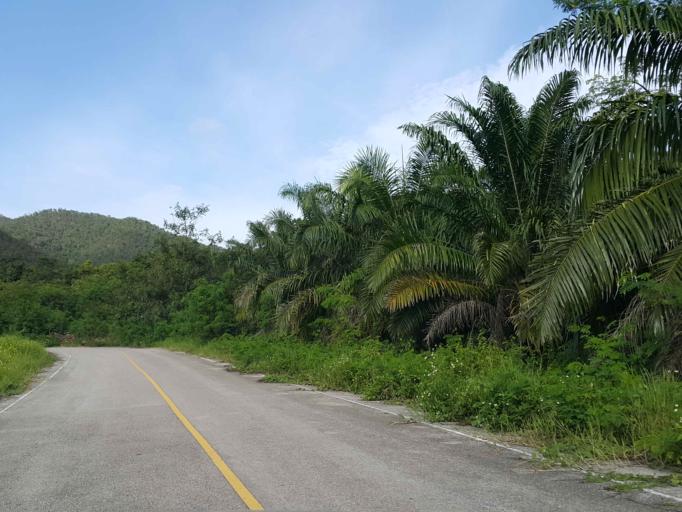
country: TH
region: Chiang Mai
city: San Sai
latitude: 18.9348
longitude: 99.1425
